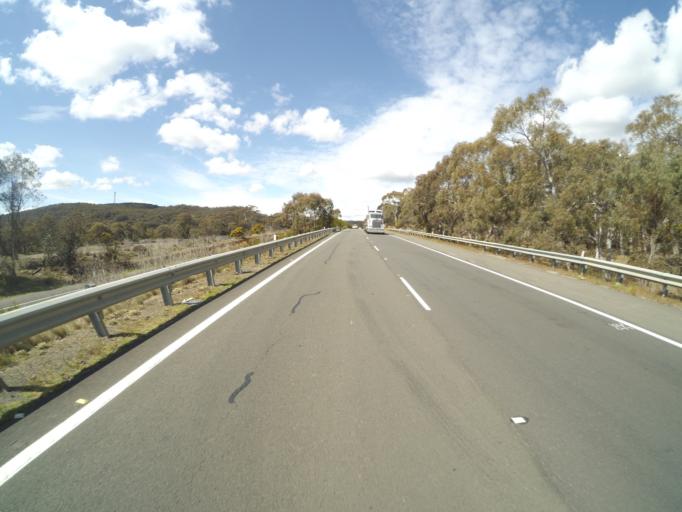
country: AU
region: New South Wales
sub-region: Goulburn Mulwaree
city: Goulburn
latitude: -34.7427
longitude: 149.9174
